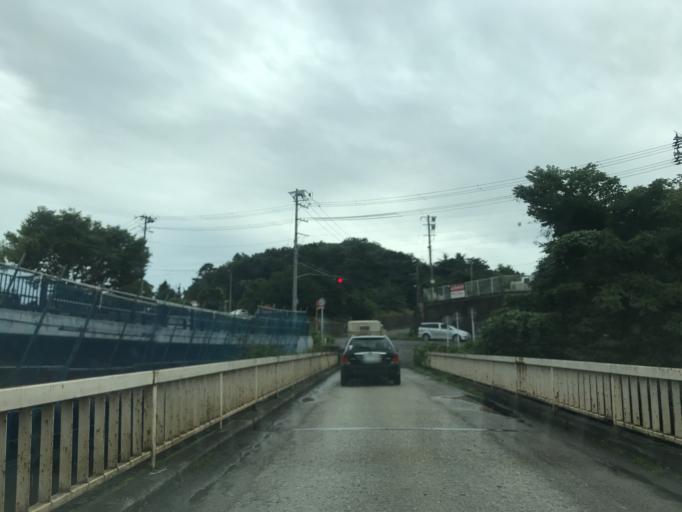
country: JP
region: Miyagi
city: Sendai-shi
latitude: 38.3161
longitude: 140.8666
